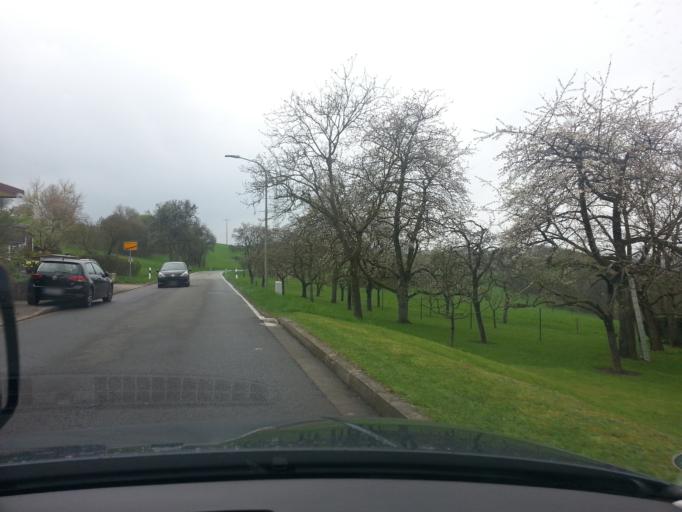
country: DE
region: Rheinland-Pfalz
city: Kashofen
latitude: 49.3234
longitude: 7.4107
